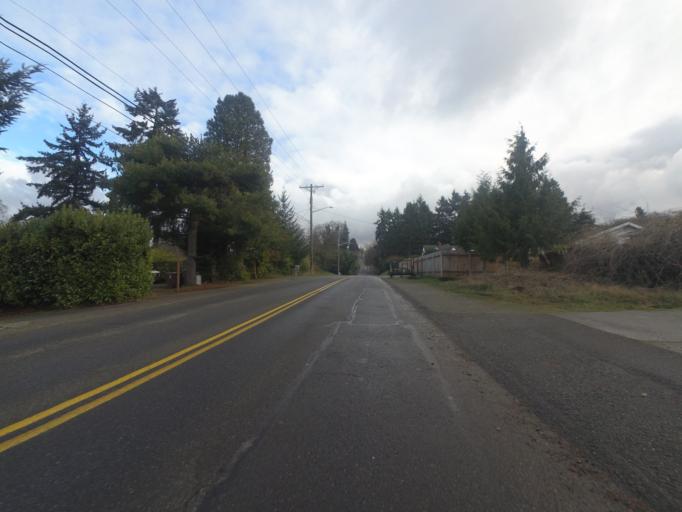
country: US
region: Washington
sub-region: Pierce County
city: University Place
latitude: 47.2427
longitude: -122.5487
